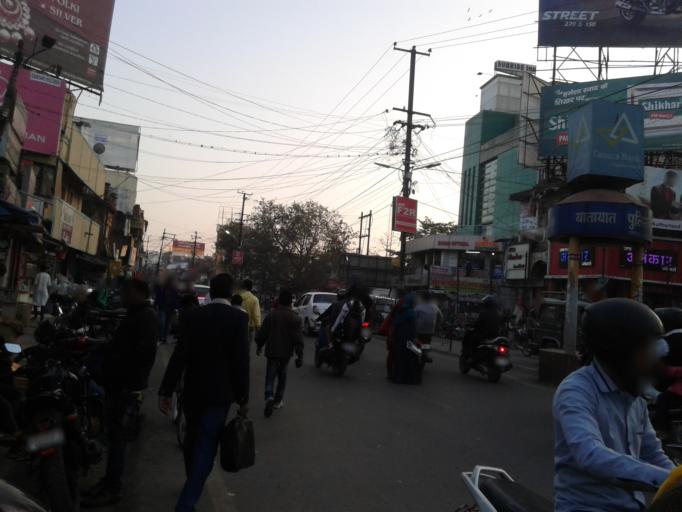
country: IN
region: Jharkhand
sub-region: Ranchi
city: Ranchi
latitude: 23.3664
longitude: 85.3249
